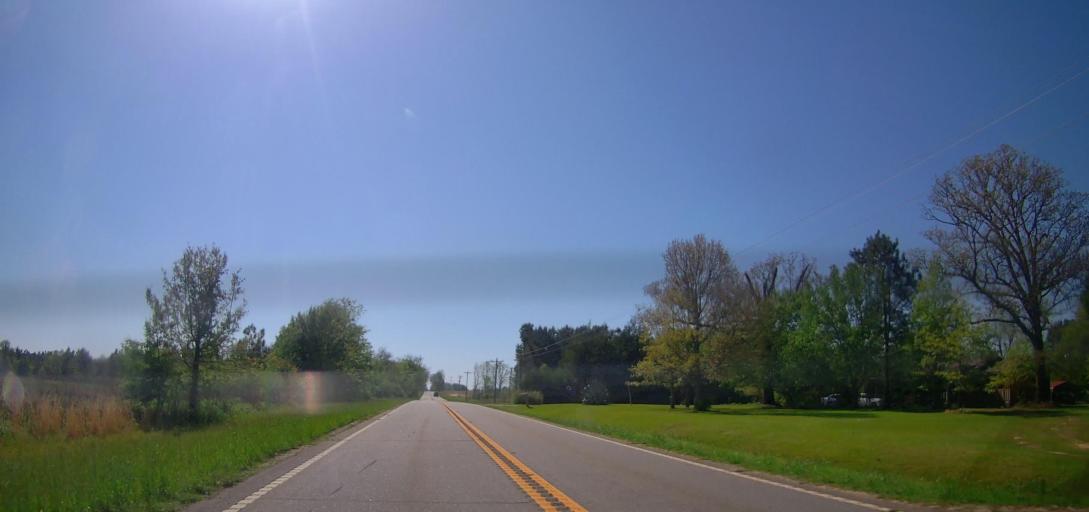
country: US
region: Georgia
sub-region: Dooly County
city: Unadilla
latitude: 32.2601
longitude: -83.6975
